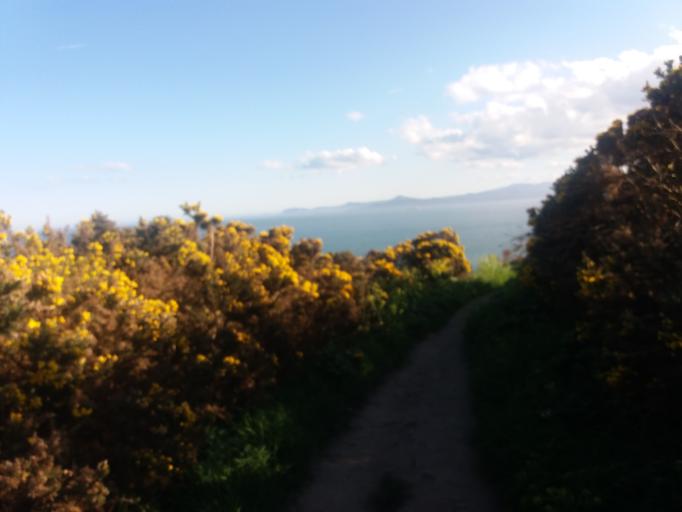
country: IE
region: Leinster
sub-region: Fingal County
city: Howth
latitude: 53.3629
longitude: -6.0721
